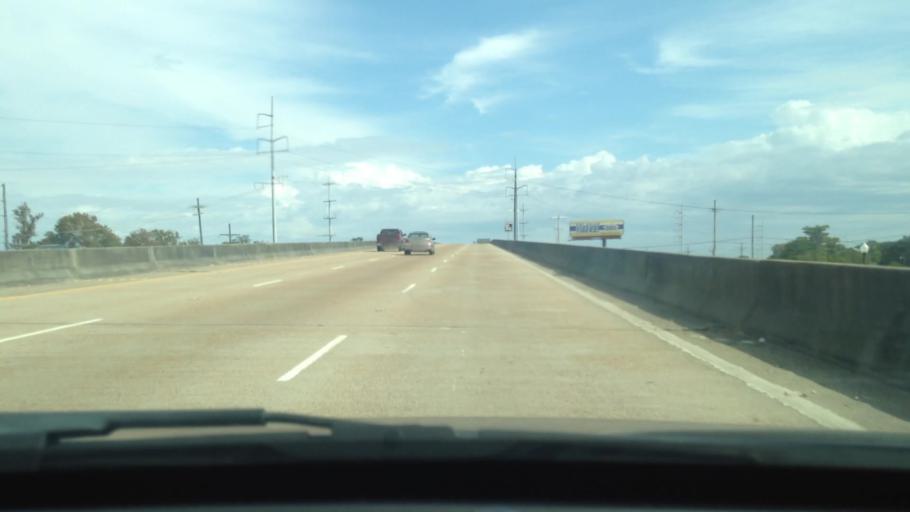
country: US
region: Louisiana
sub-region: Jefferson Parish
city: Metairie Terrace
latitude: 29.9699
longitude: -90.1754
